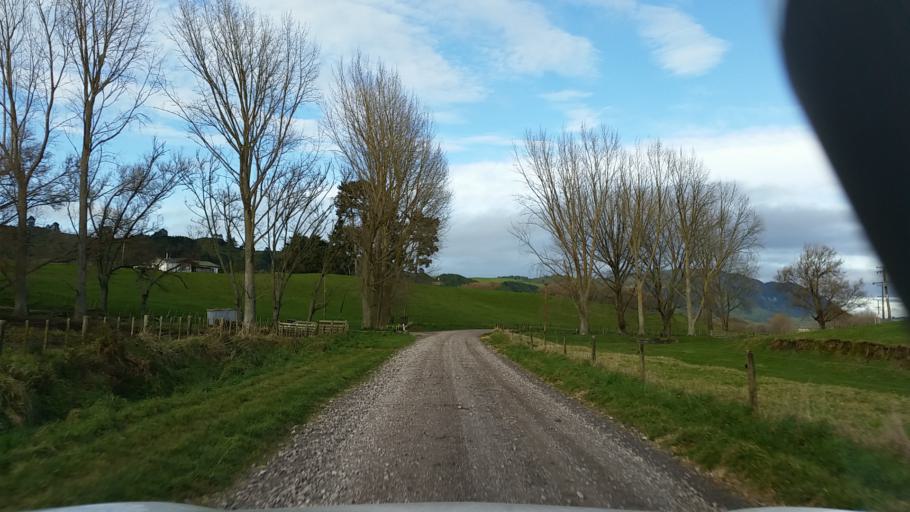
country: NZ
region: Bay of Plenty
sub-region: Rotorua District
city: Rotorua
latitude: -38.3155
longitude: 176.3019
